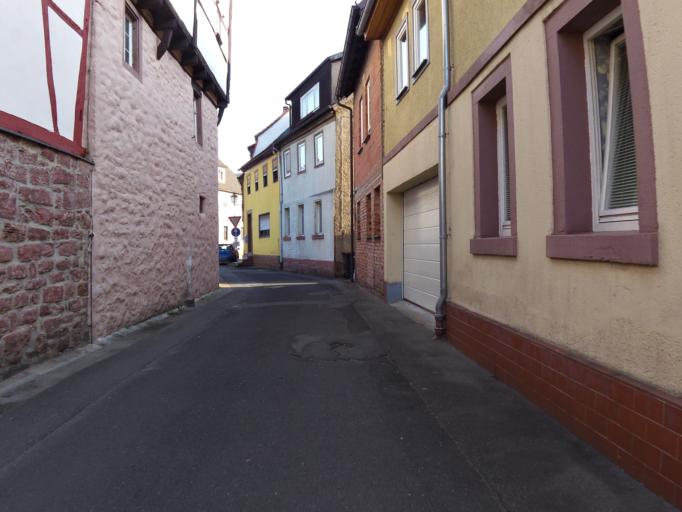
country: DE
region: Bavaria
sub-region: Regierungsbezirk Unterfranken
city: Weilbach
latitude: 49.6453
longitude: 9.2169
